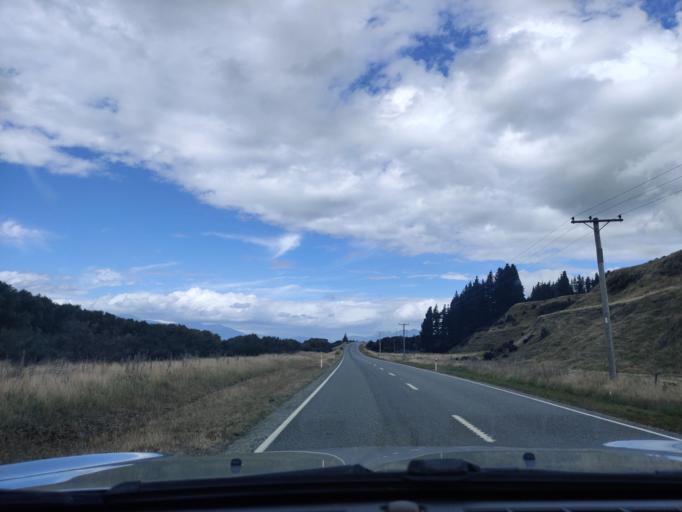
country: NZ
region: Canterbury
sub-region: Hurunui District
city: Amberley
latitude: -42.5697
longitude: 172.6908
